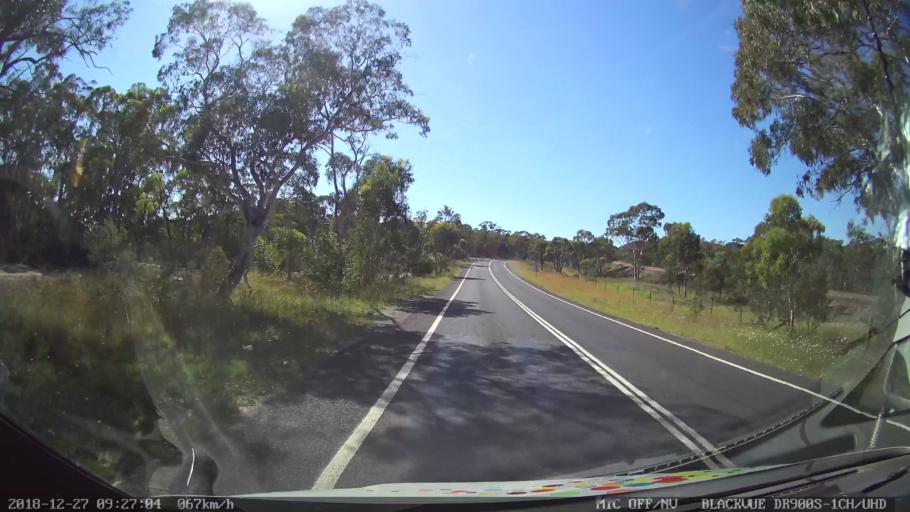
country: AU
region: New South Wales
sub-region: Lithgow
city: Portland
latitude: -33.1495
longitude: 149.9909
